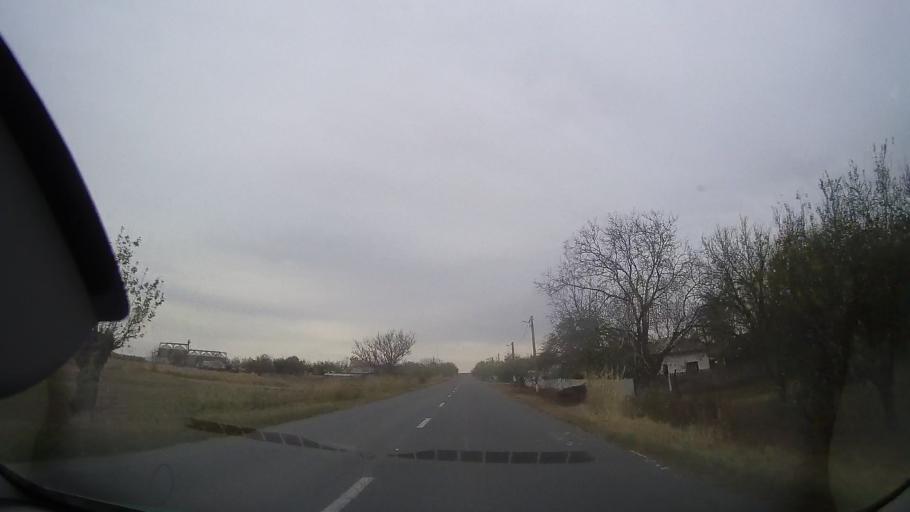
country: RO
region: Ialomita
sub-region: Comuna Milosesti
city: Milosesti
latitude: 44.7550
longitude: 27.2123
